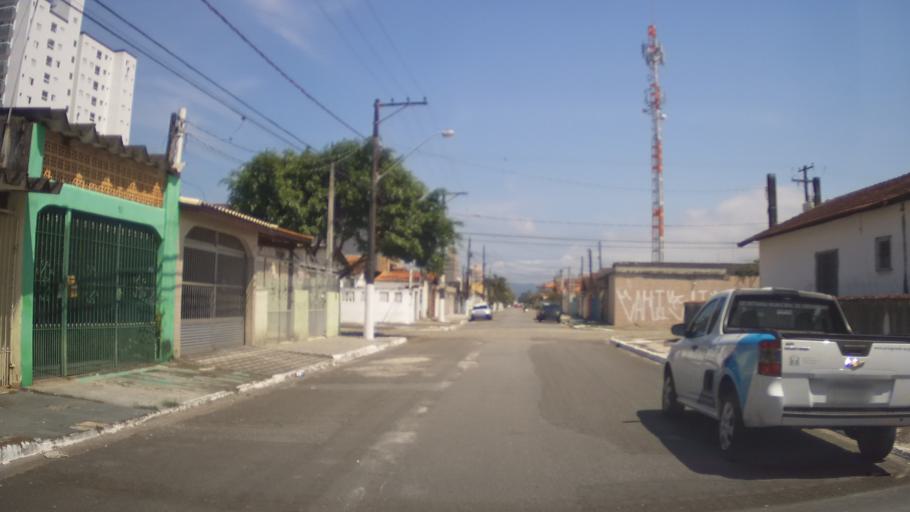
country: BR
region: Sao Paulo
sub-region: Praia Grande
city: Praia Grande
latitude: -24.0128
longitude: -46.4409
